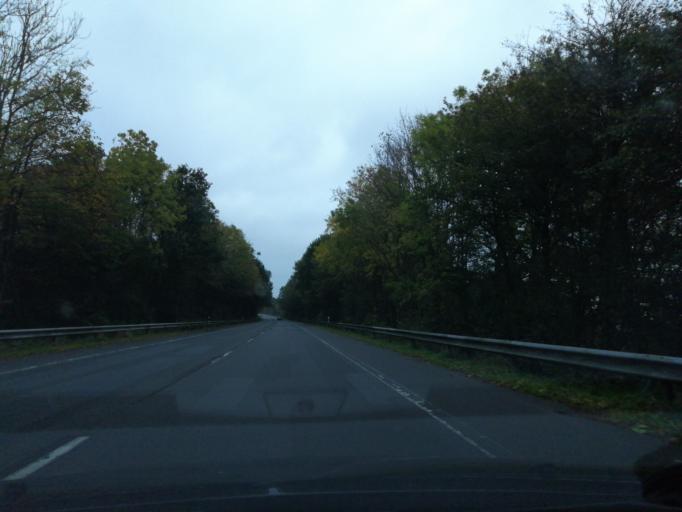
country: DE
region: Lower Saxony
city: Fedderwarden
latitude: 53.5597
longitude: 8.0514
